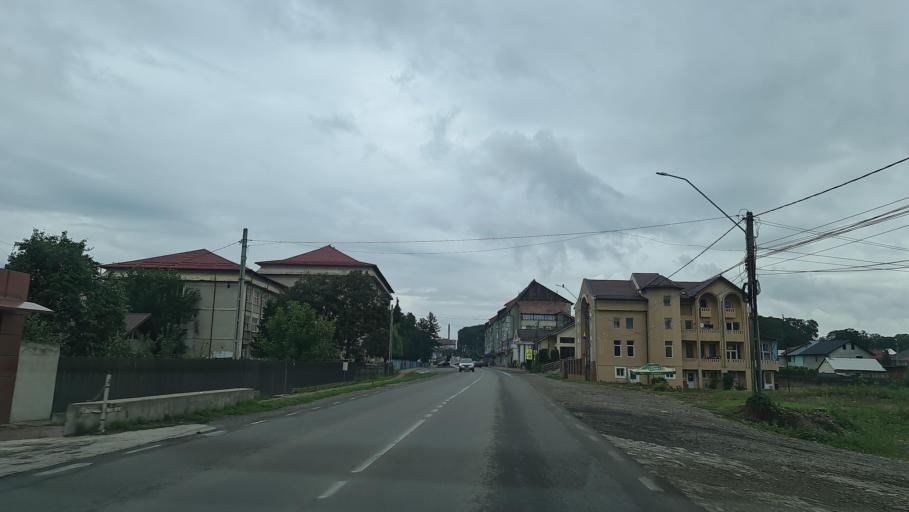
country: RO
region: Neamt
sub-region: Comuna Roznov
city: Chintinici
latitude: 46.8350
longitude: 26.5016
